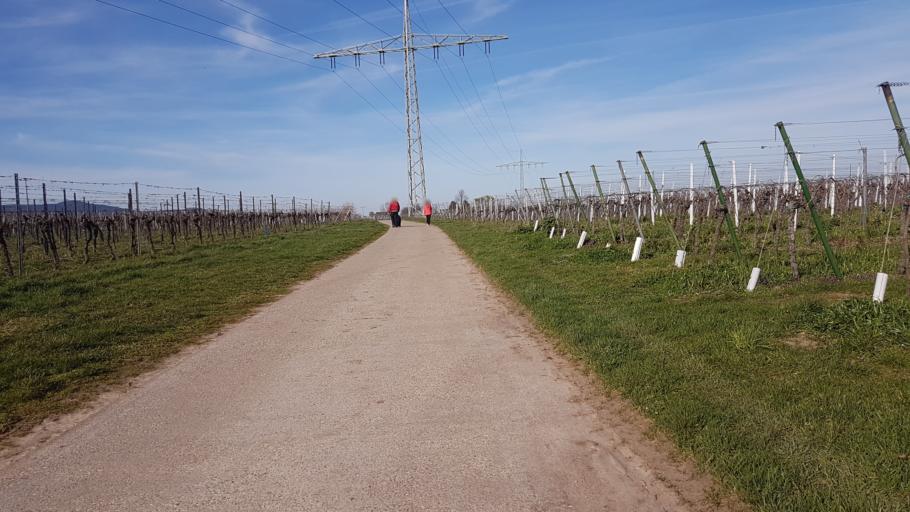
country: DE
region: Rheinland-Pfalz
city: Kirrweiler
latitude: 49.2989
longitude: 8.1502
